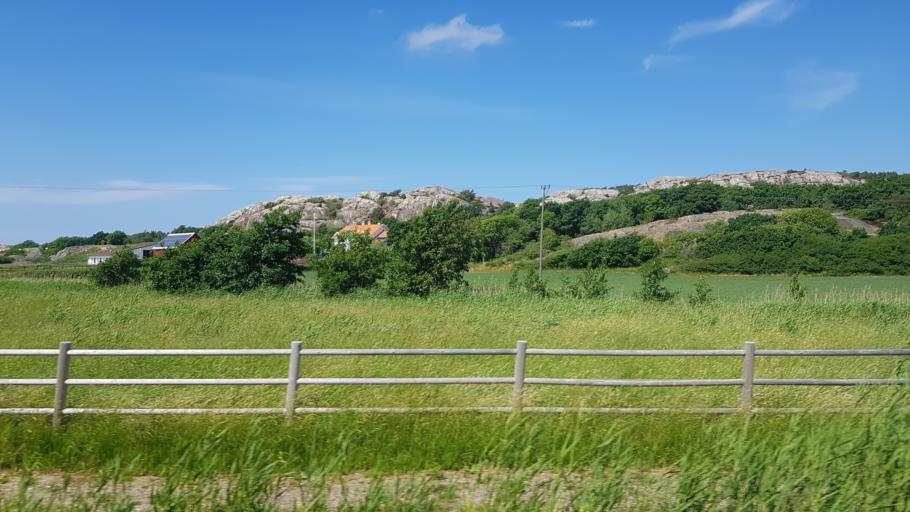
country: SE
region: Vaestra Goetaland
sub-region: Tjorns Kommun
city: Skaerhamn
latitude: 57.9737
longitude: 11.5607
